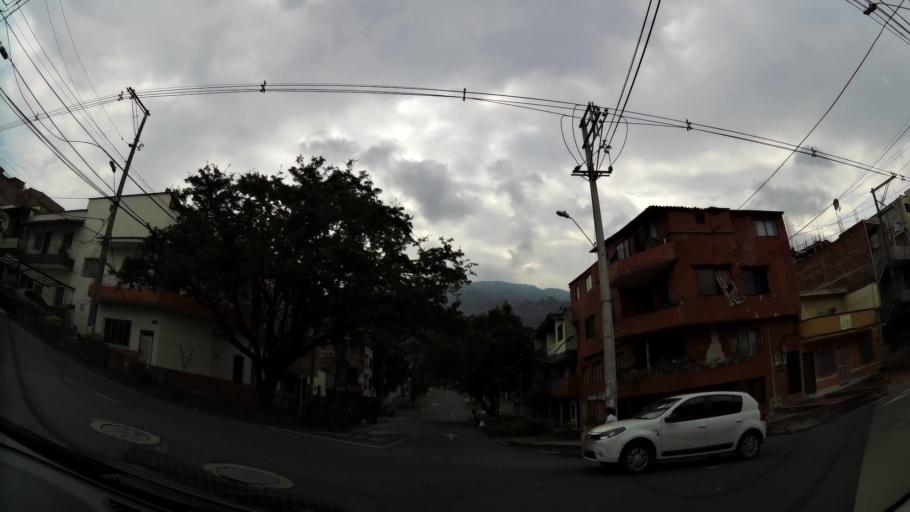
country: CO
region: Antioquia
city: Medellin
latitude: 6.2847
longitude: -75.5616
